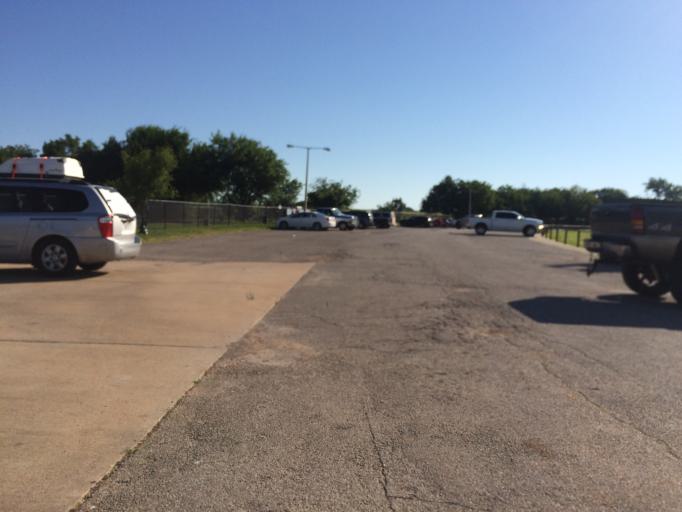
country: US
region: Oklahoma
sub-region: Cleveland County
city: Norman
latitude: 35.2377
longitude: -97.4270
